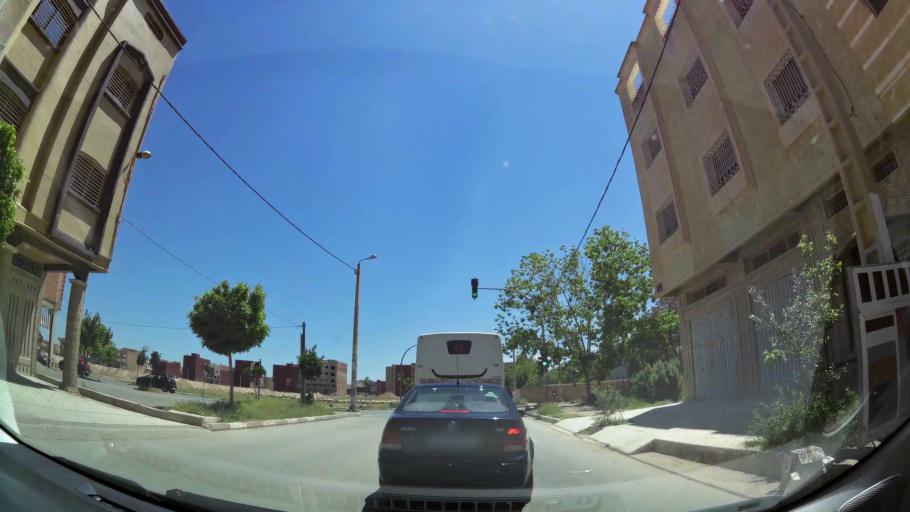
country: MA
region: Oriental
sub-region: Oujda-Angad
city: Oujda
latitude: 34.6706
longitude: -1.8825
